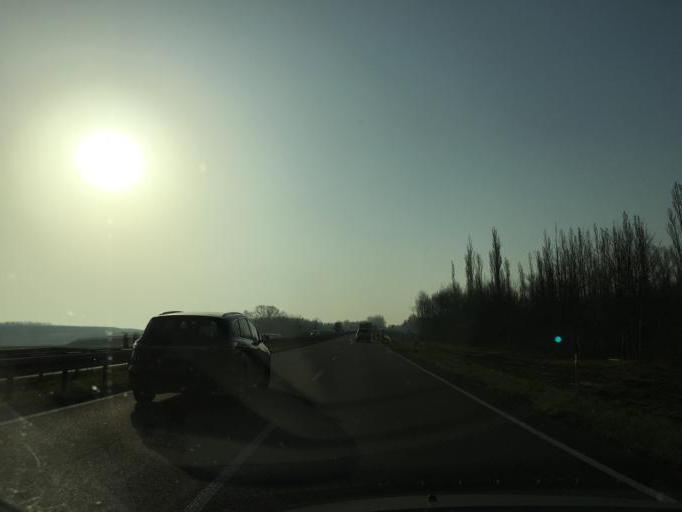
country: DE
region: Saxony
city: Rotha
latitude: 51.2056
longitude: 12.4108
